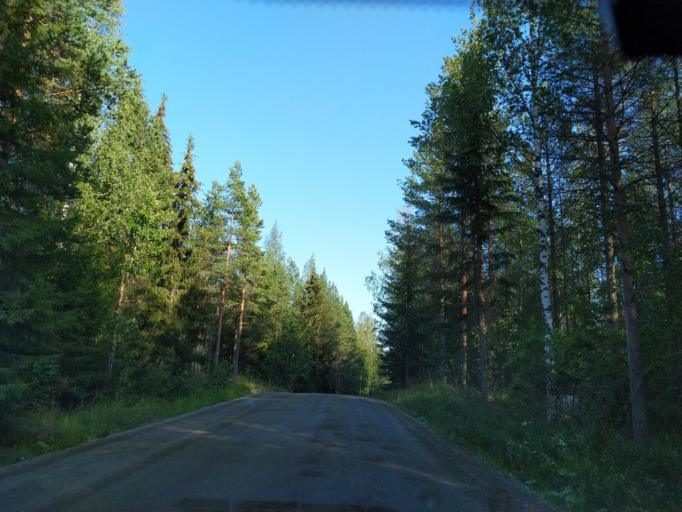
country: FI
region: Central Finland
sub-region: Jaemsae
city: Kuhmoinen
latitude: 61.6095
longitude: 25.1260
